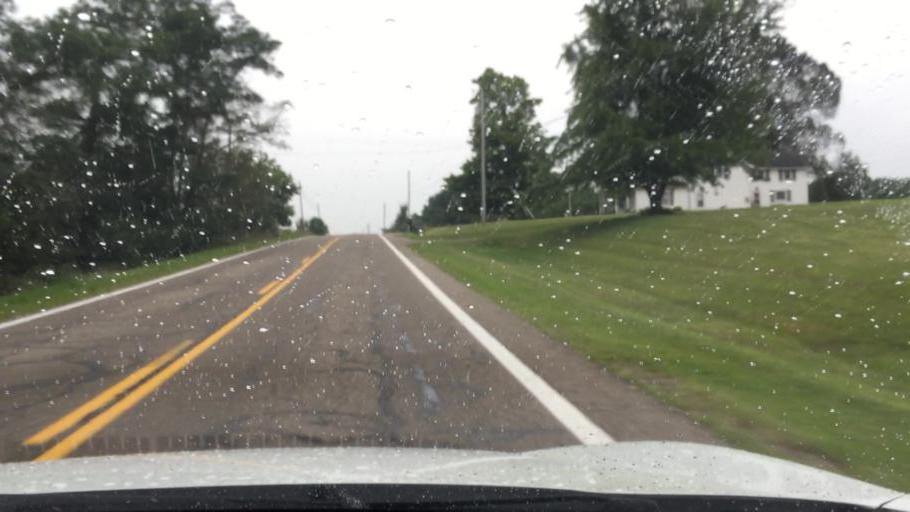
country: US
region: Ohio
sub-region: Champaign County
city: Mechanicsburg
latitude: 40.0140
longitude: -83.6308
